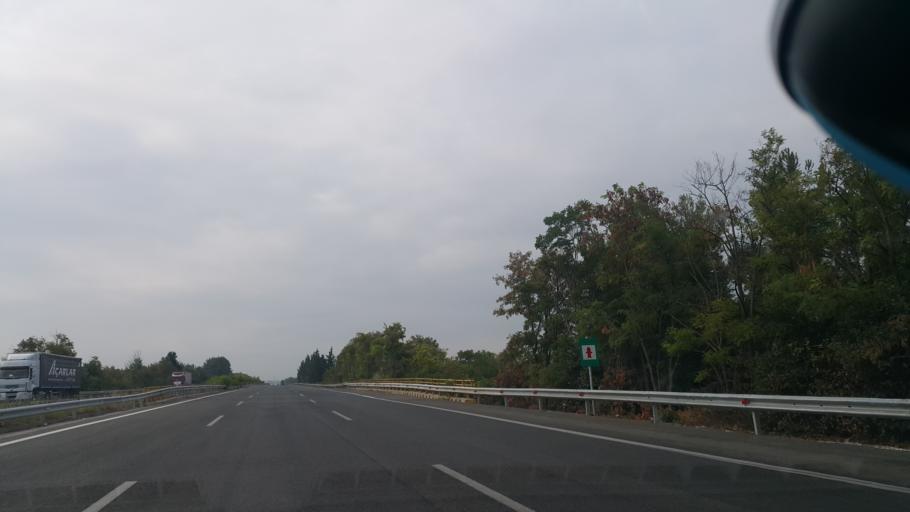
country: GR
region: Central Macedonia
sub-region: Nomos Pierias
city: Aiginio
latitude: 40.4883
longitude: 22.5654
